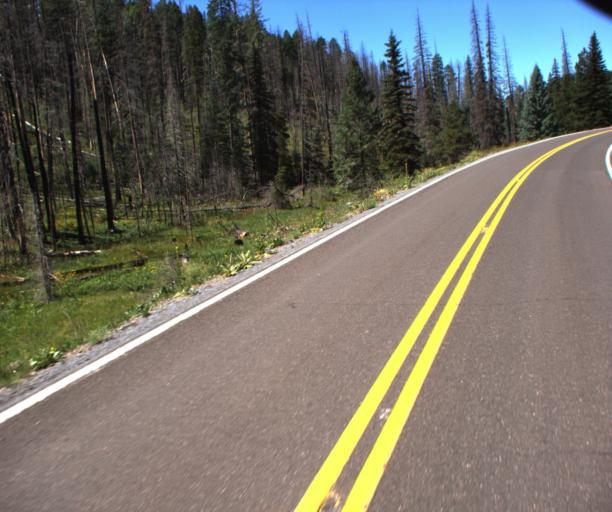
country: US
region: Arizona
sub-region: Apache County
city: Eagar
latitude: 33.6465
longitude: -109.2927
